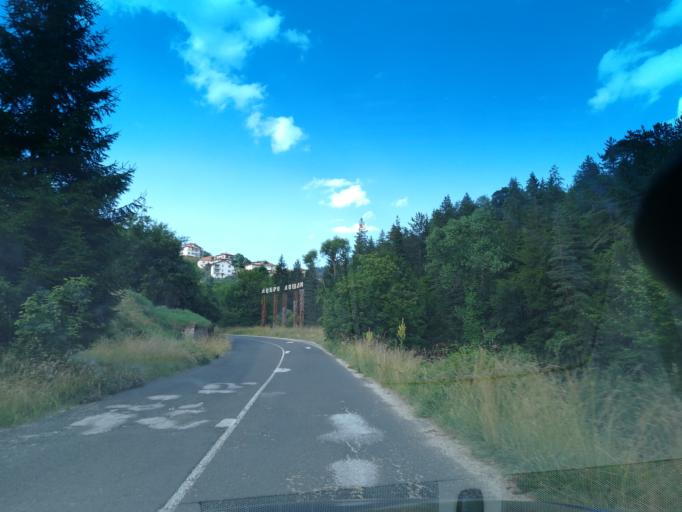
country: BG
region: Smolyan
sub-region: Obshtina Smolyan
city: Smolyan
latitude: 41.6520
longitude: 24.7720
